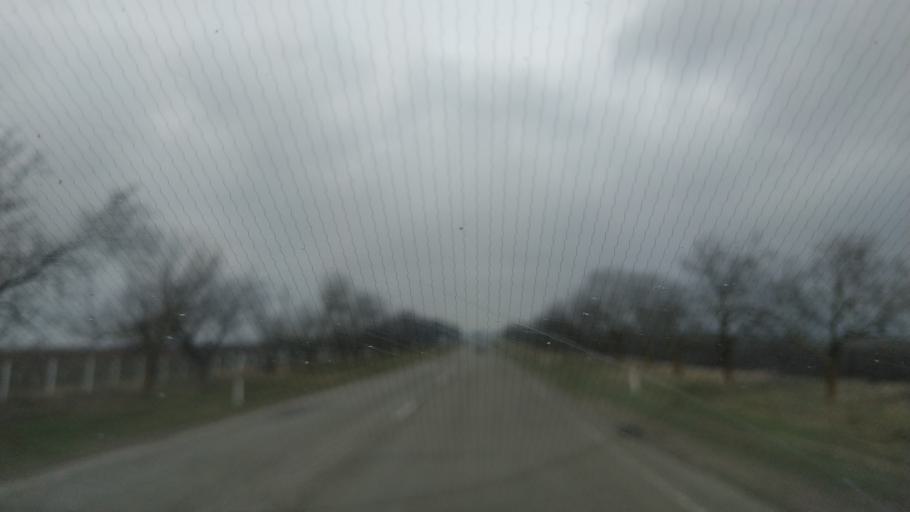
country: MD
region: Gagauzia
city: Comrat
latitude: 46.2639
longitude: 28.7428
